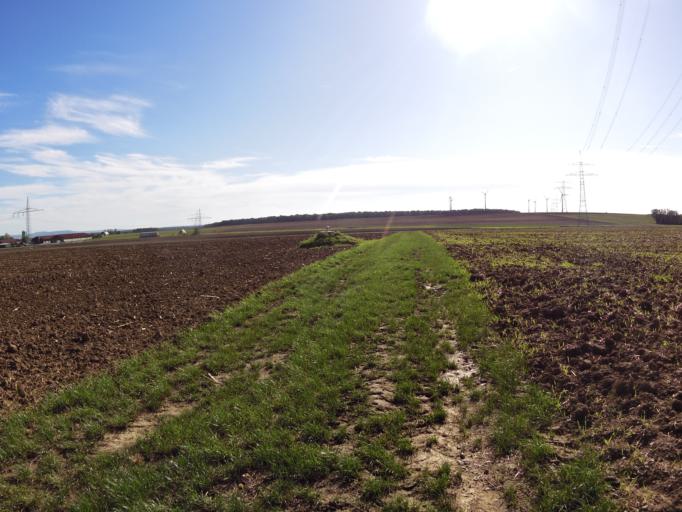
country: DE
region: Bavaria
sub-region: Regierungsbezirk Unterfranken
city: Theilheim
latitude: 49.7467
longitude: 10.0540
